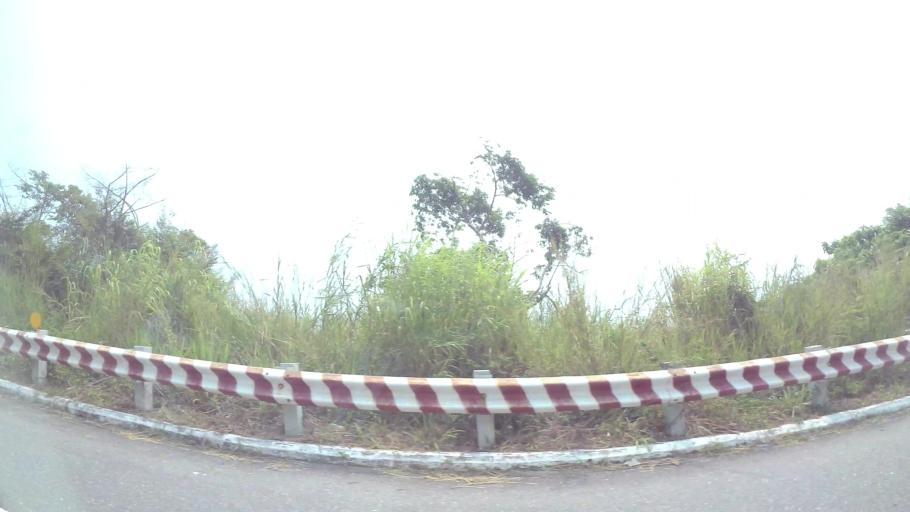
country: VN
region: Da Nang
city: Son Tra
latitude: 16.0981
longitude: 108.3049
